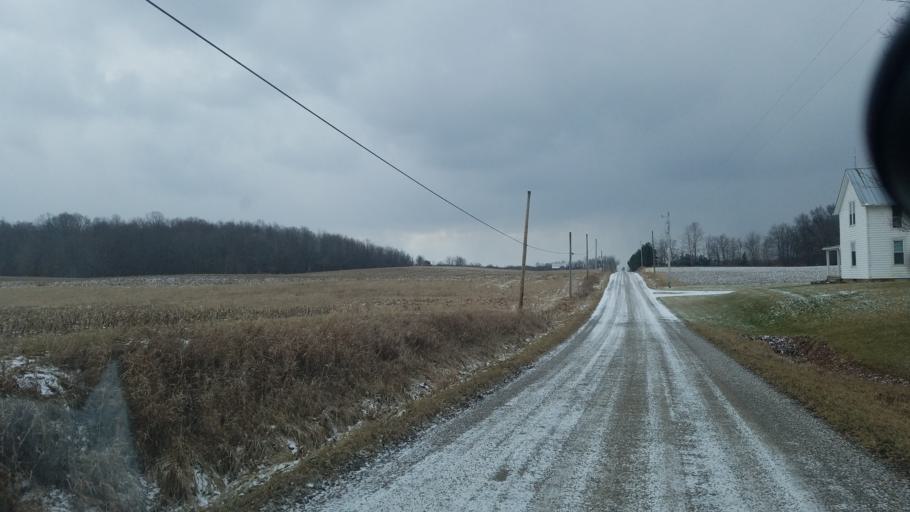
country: US
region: Ohio
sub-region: Morrow County
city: Mount Gilead
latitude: 40.5960
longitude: -82.7907
